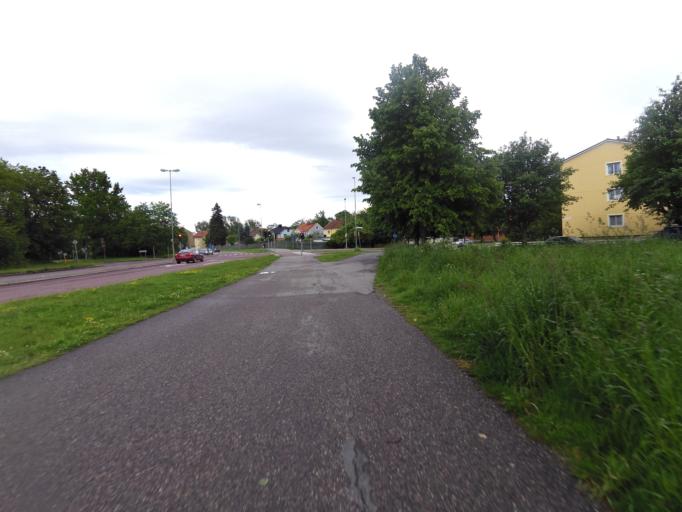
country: SE
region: Gaevleborg
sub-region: Gavle Kommun
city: Gavle
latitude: 60.6783
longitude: 17.1270
